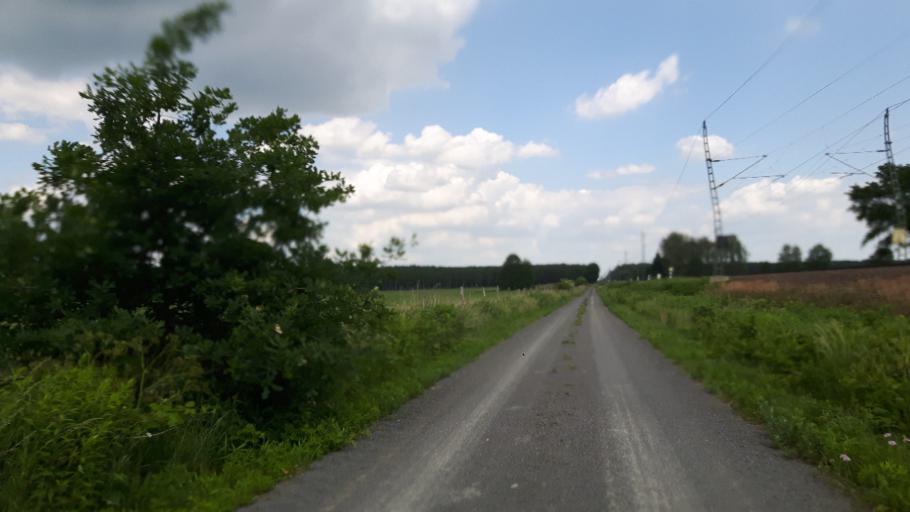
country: DE
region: Saxony-Anhalt
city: Radis
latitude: 51.7614
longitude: 12.5138
